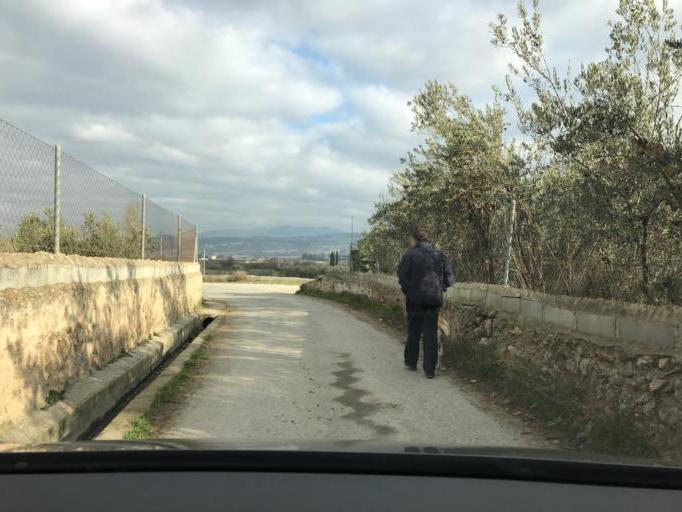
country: ES
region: Andalusia
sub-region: Provincia de Granada
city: Zubia
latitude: 37.1255
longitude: -3.5935
